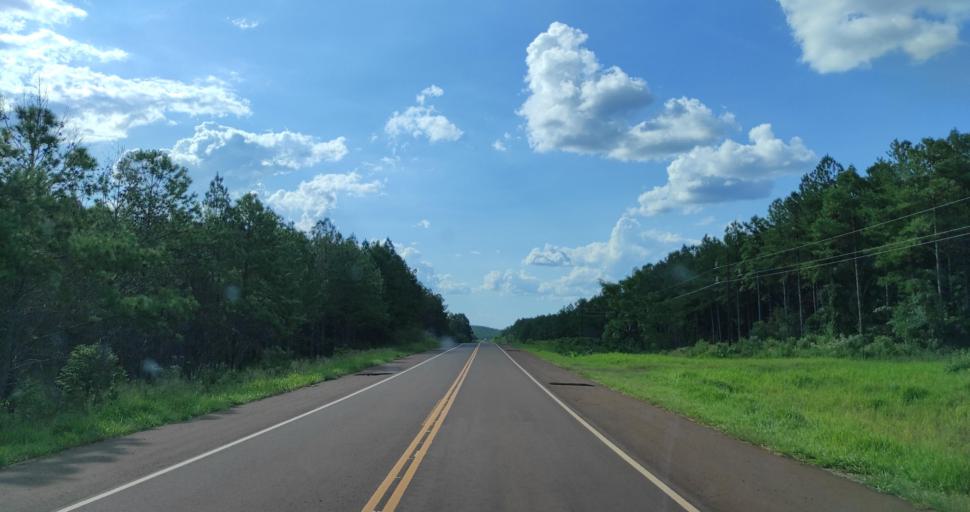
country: AR
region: Misiones
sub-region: Departamento de San Pedro
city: San Pedro
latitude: -26.3672
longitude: -53.9458
